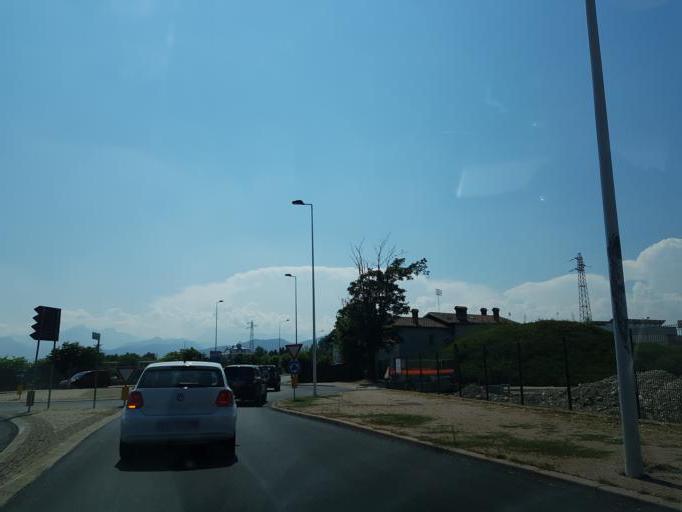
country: IT
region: Piedmont
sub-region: Provincia di Cuneo
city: Cuneo
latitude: 44.3961
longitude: 7.5343
